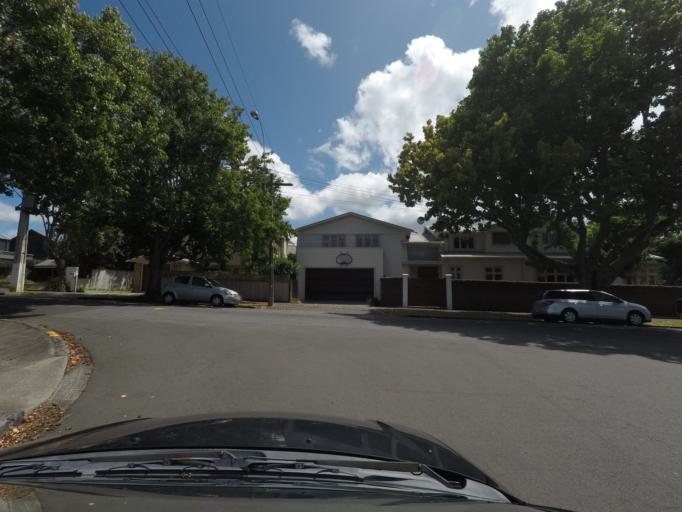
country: NZ
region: Auckland
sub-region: Auckland
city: Rosebank
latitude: -36.8569
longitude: 174.7074
